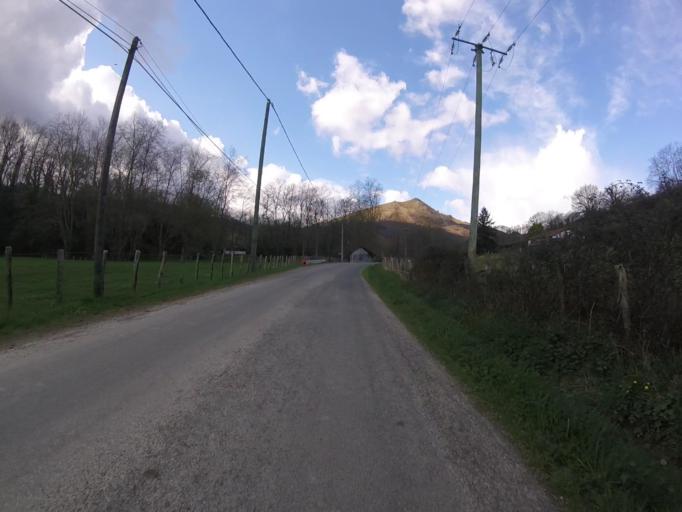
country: FR
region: Aquitaine
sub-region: Departement des Pyrenees-Atlantiques
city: Sare
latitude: 43.2819
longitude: -1.5908
